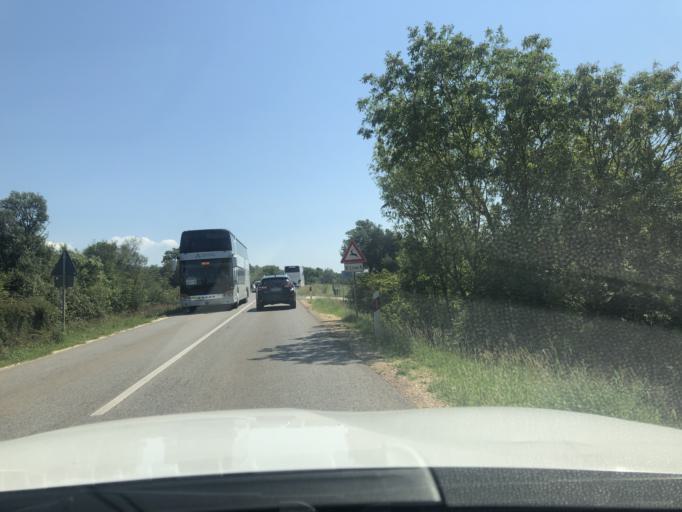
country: HR
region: Istarska
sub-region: Grad Rovinj
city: Rovinj
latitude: 45.0473
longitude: 13.7438
